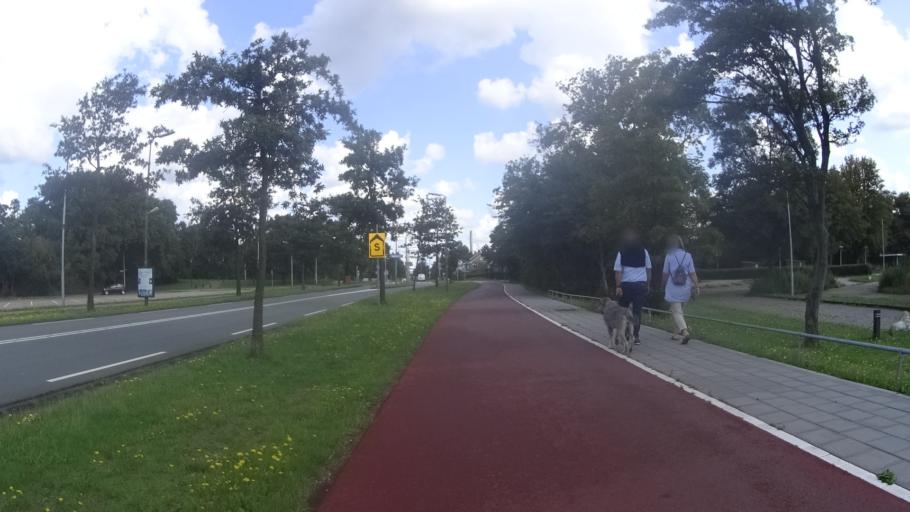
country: NL
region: North Holland
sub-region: Gemeente Velsen
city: Velsen-Zuid
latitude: 52.4555
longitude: 4.6336
